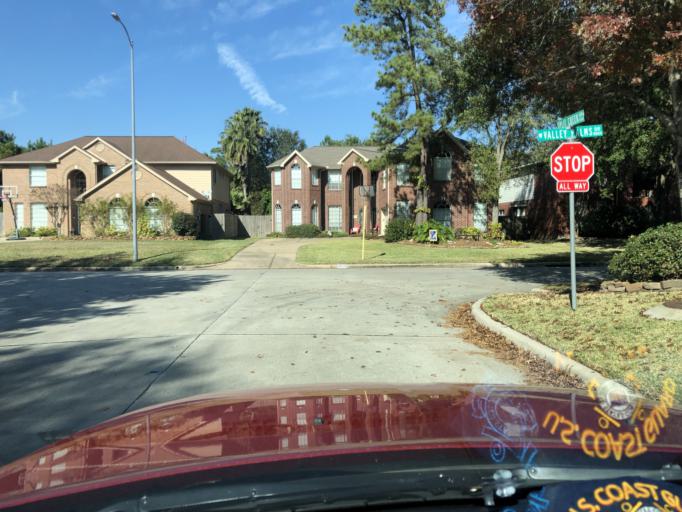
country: US
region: Texas
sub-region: Harris County
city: Tomball
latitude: 30.0225
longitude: -95.5547
